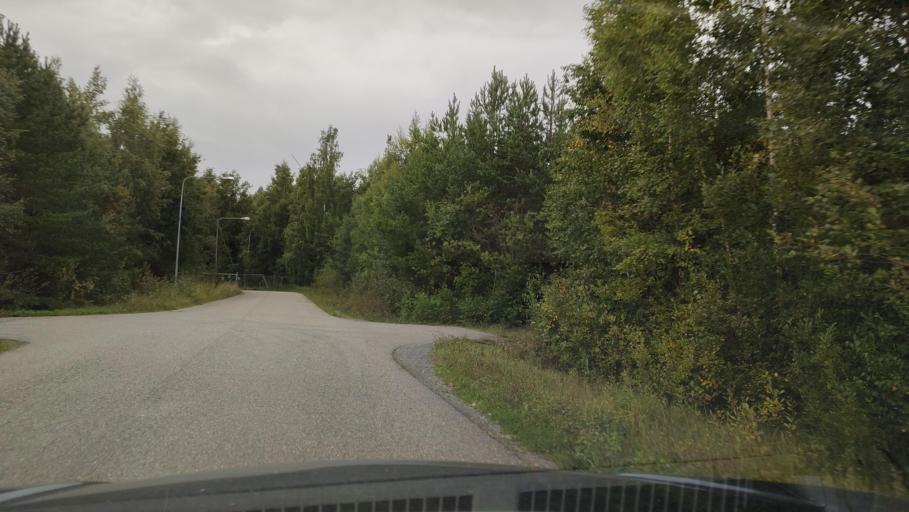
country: FI
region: Ostrobothnia
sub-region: Sydosterbotten
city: Kristinestad
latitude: 62.2535
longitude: 21.3295
